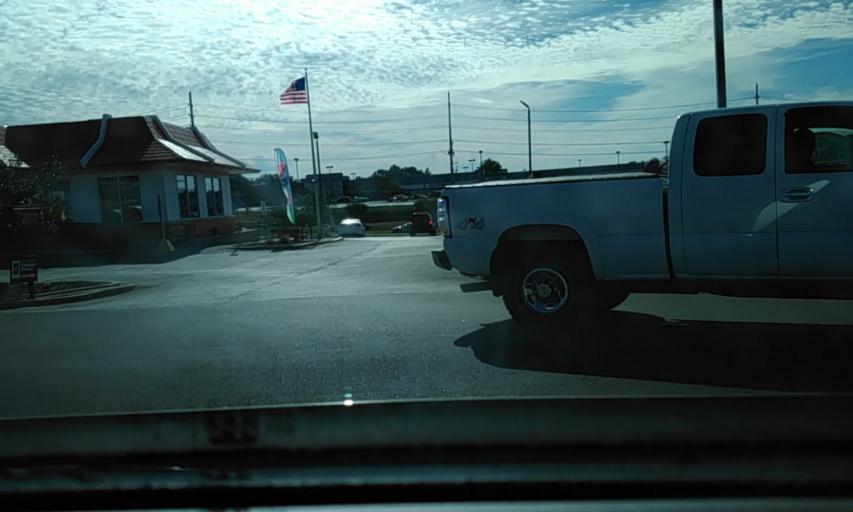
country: US
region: Missouri
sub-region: Saint Louis County
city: Mehlville
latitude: 38.5010
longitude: -90.3340
